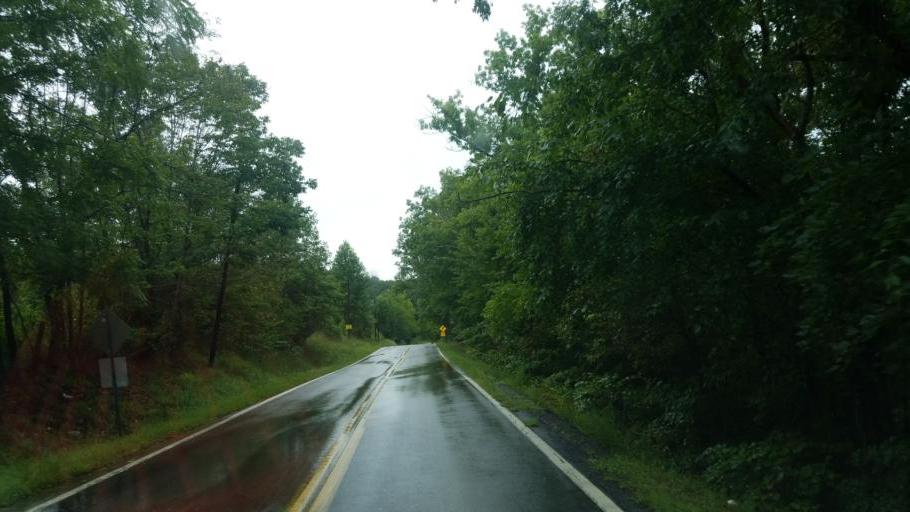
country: US
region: Ohio
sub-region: Adams County
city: West Union
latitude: 38.7879
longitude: -83.5413
